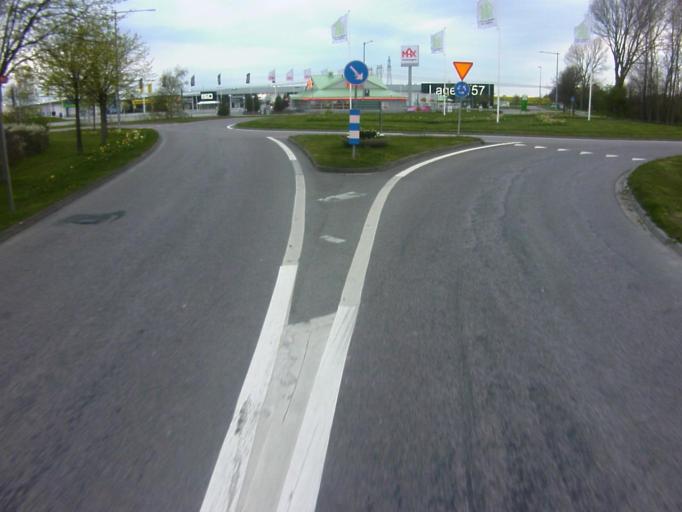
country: SE
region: Skane
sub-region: Kavlinge Kommun
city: Hofterup
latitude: 55.7706
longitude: 12.9900
